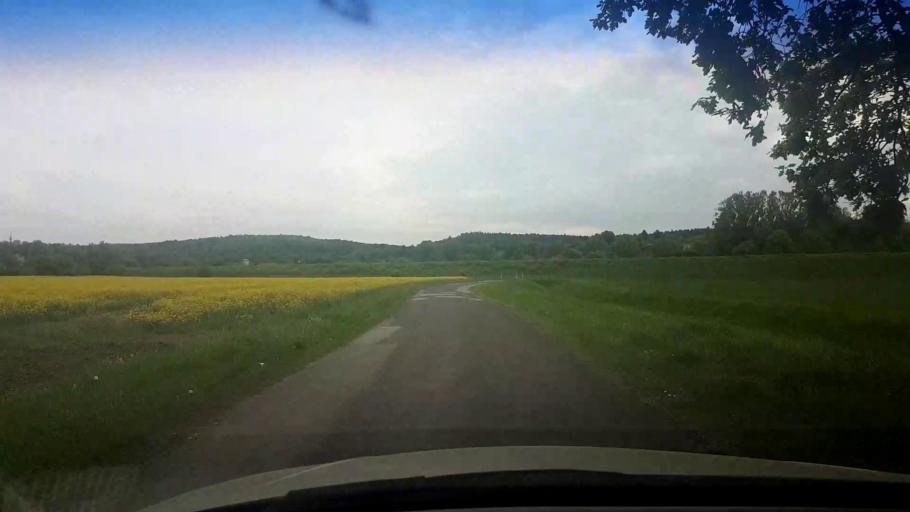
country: DE
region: Bavaria
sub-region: Upper Franconia
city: Bamberg
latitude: 49.8754
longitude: 10.9133
